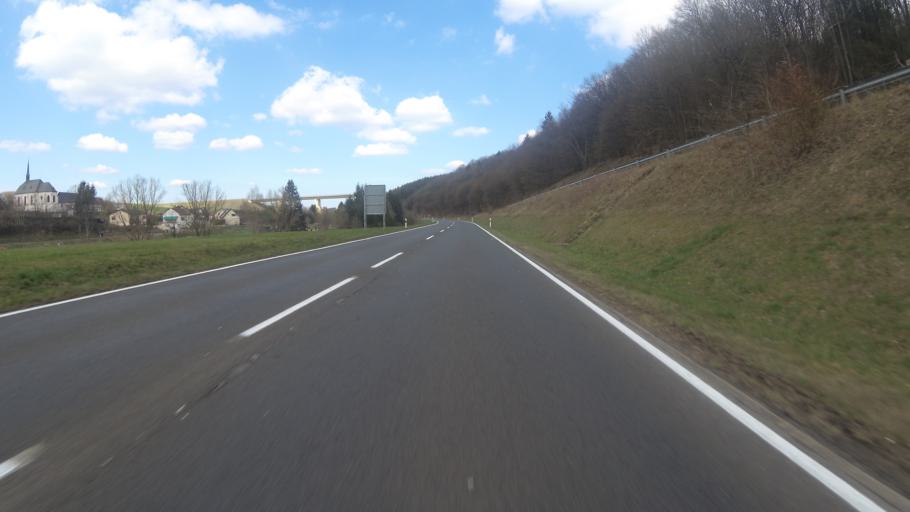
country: DE
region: Rheinland-Pfalz
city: Horscheid
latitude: 50.2214
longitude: 6.8457
